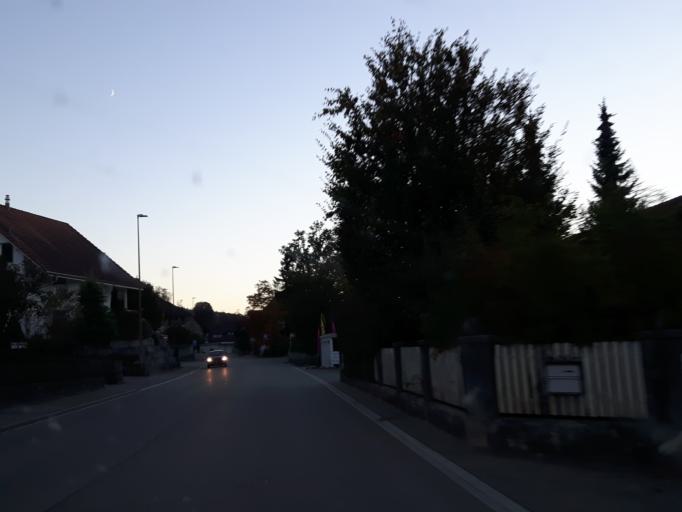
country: CH
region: Bern
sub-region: Oberaargau
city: Lotzwil
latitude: 47.1874
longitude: 7.7590
